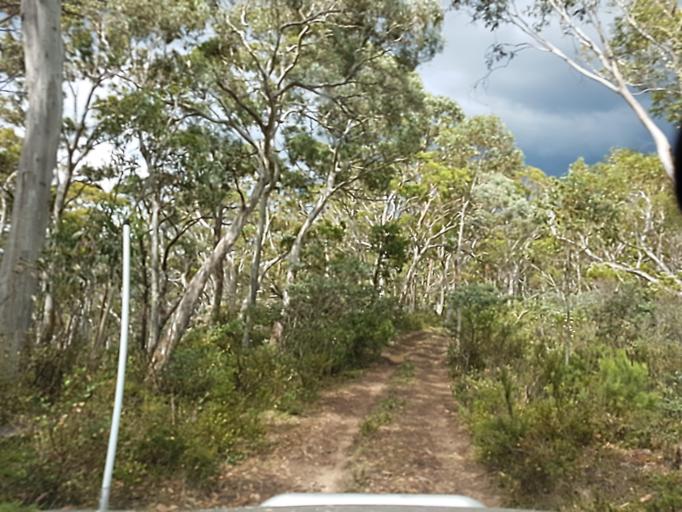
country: AU
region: New South Wales
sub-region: Snowy River
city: Jindabyne
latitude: -36.8793
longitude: 148.1876
